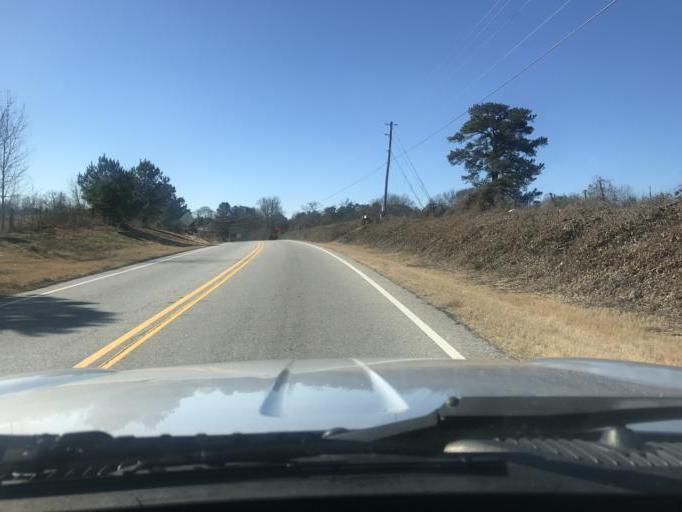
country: US
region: Georgia
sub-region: Barrow County
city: Winder
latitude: 33.9414
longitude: -83.7608
